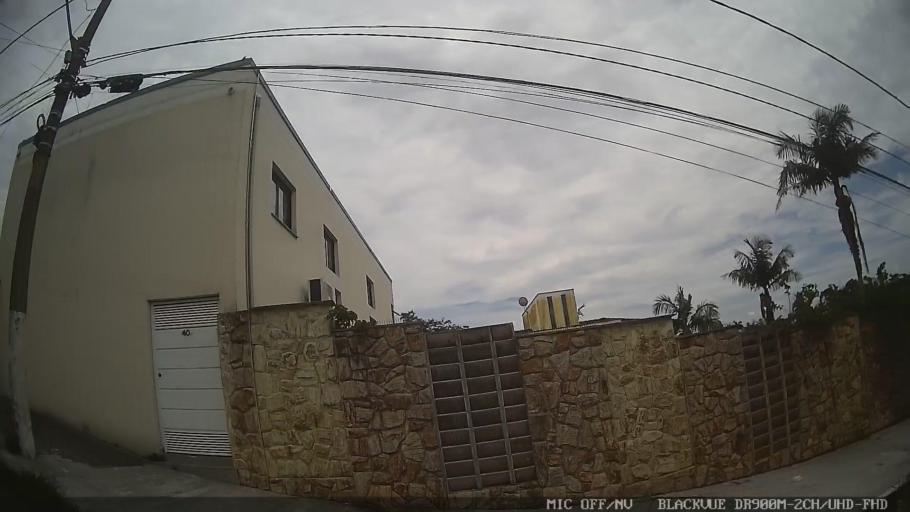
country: BR
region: Sao Paulo
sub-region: Ribeirao Pires
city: Ribeirao Pires
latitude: -23.7197
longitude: -46.4147
